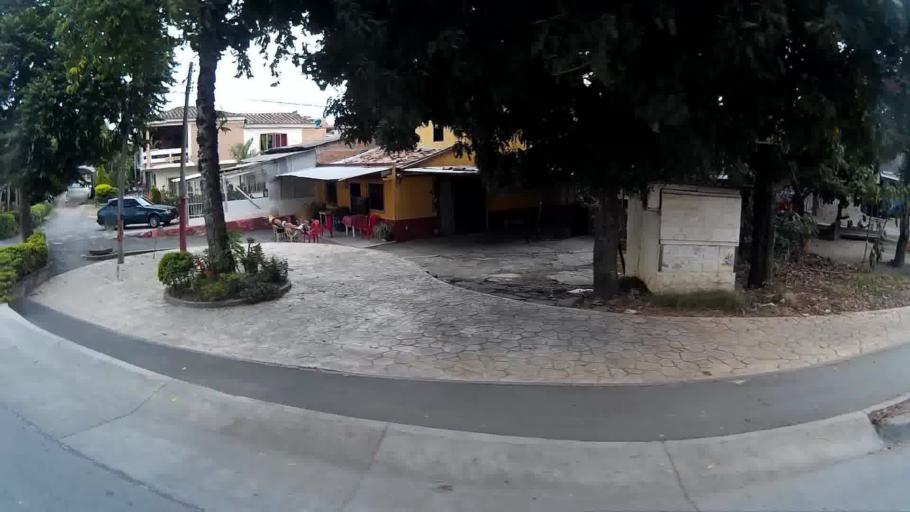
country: CO
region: Risaralda
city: La Virginia
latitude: 4.8895
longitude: -75.8707
